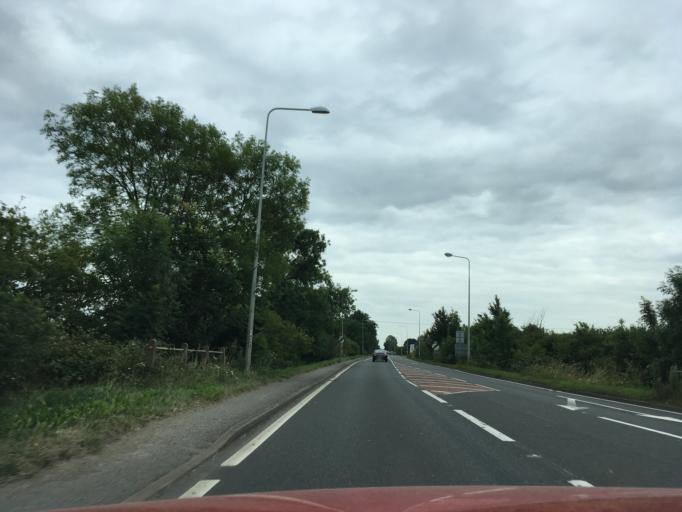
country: GB
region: England
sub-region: Central Bedfordshire
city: Hockliffe
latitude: 51.9233
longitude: -0.5746
